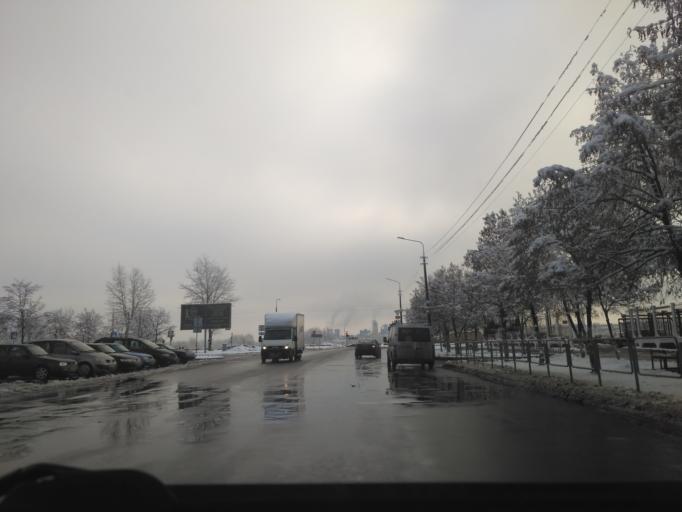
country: BY
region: Minsk
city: Horad Barysaw
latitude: 54.2390
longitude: 28.5123
